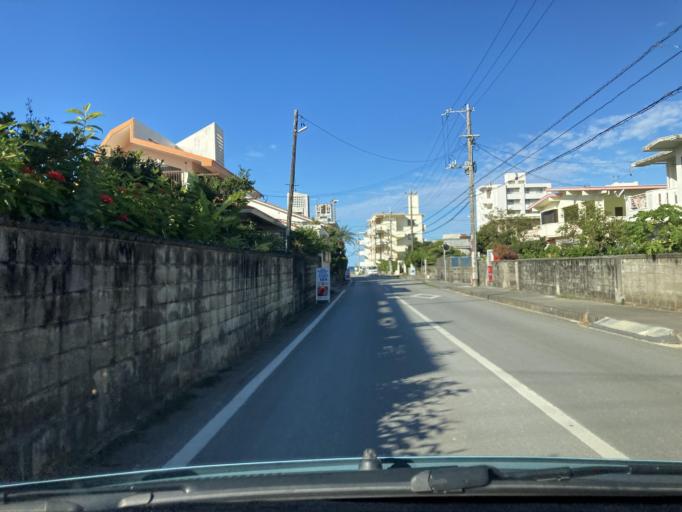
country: JP
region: Okinawa
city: Chatan
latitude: 26.3707
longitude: 127.7382
